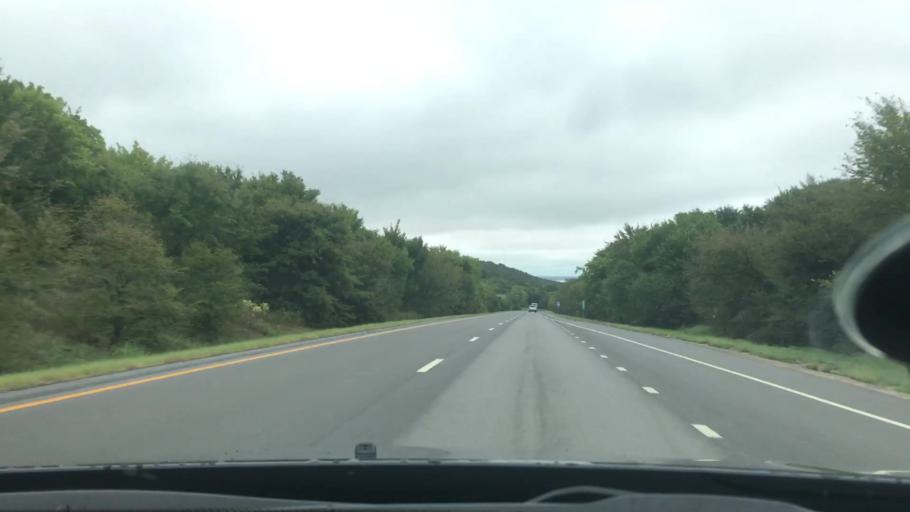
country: US
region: Oklahoma
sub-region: Okmulgee County
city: Morris
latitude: 35.4377
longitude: -95.7880
